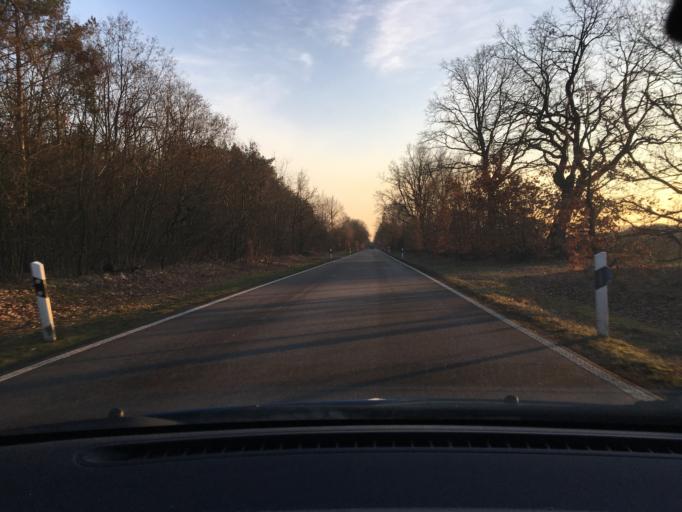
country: DE
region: Schleswig-Holstein
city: Langenlehsten
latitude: 53.5137
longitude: 10.7440
